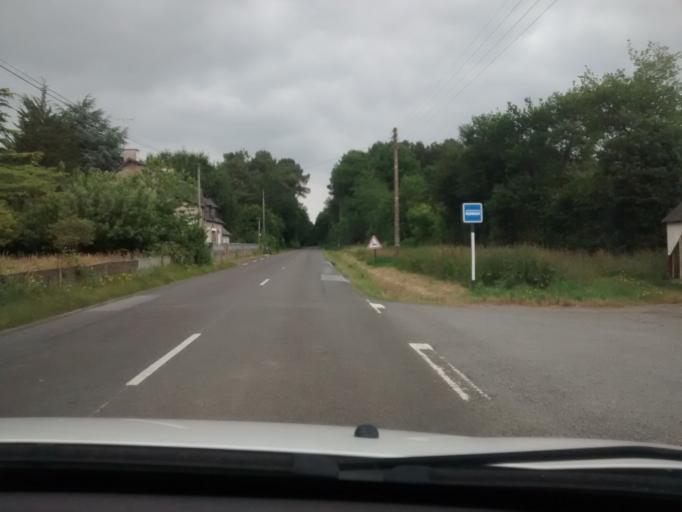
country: FR
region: Brittany
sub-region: Departement d'Ille-et-Vilaine
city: Servon-sur-Vilaine
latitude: 48.1396
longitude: -1.4518
